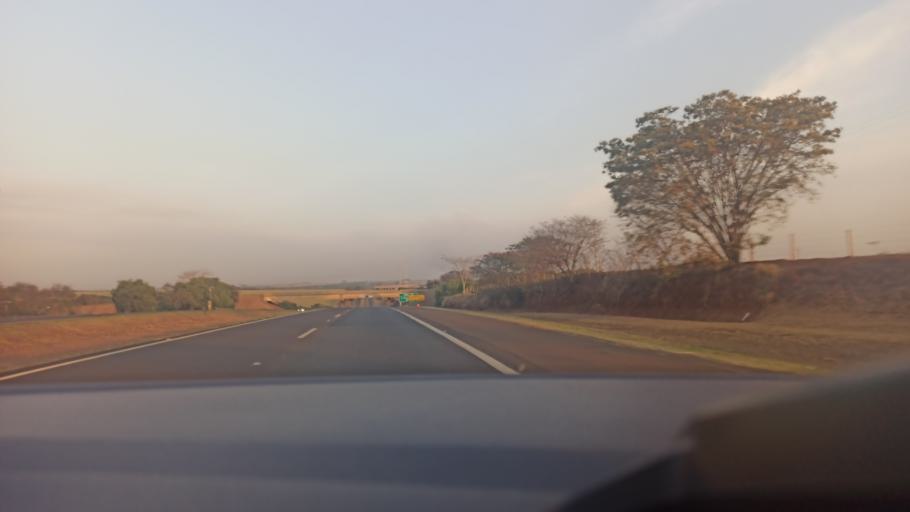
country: BR
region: Sao Paulo
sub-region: Taquaritinga
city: Taquaritinga
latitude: -21.4142
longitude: -48.6877
